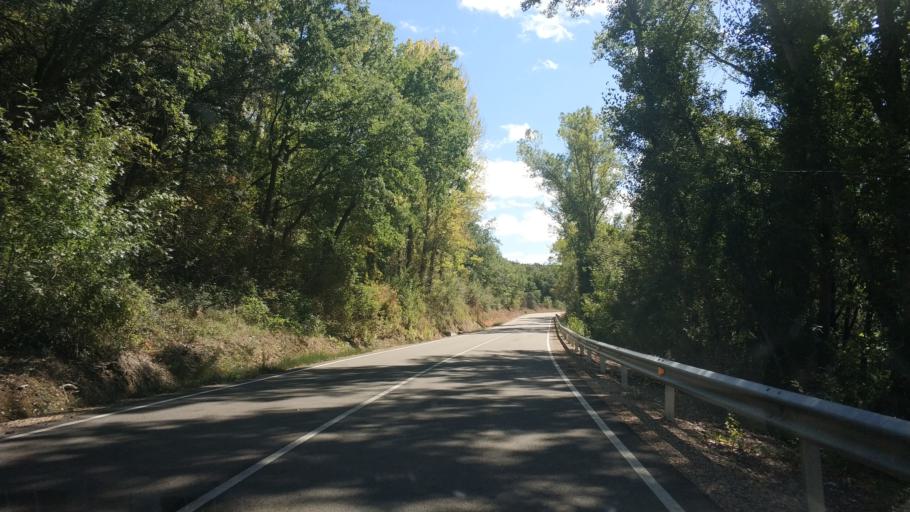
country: ES
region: Castille and Leon
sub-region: Provincia de Burgos
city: Puentedura
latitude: 42.0514
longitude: -3.5516
